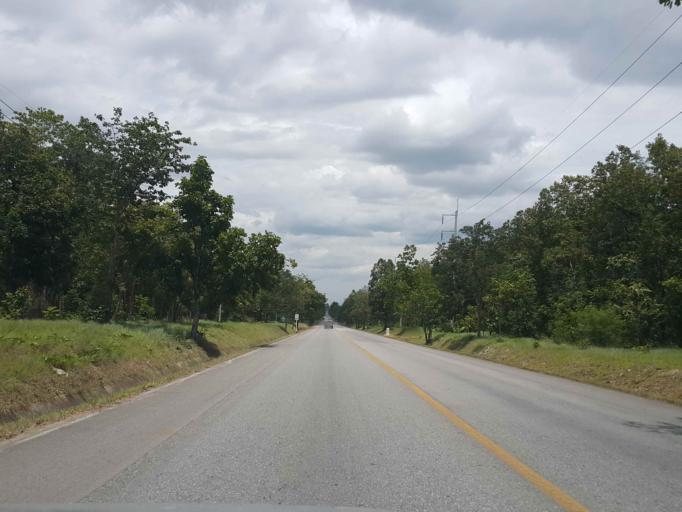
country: TH
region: Chiang Mai
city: Doi Lo
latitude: 18.4139
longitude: 98.8499
